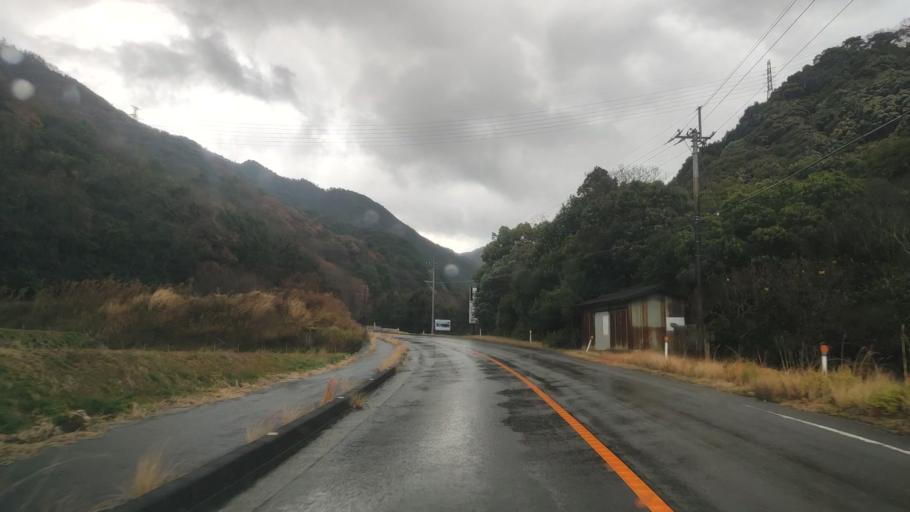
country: JP
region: Tokushima
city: Kamojimacho-jogejima
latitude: 34.1919
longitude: 134.3343
